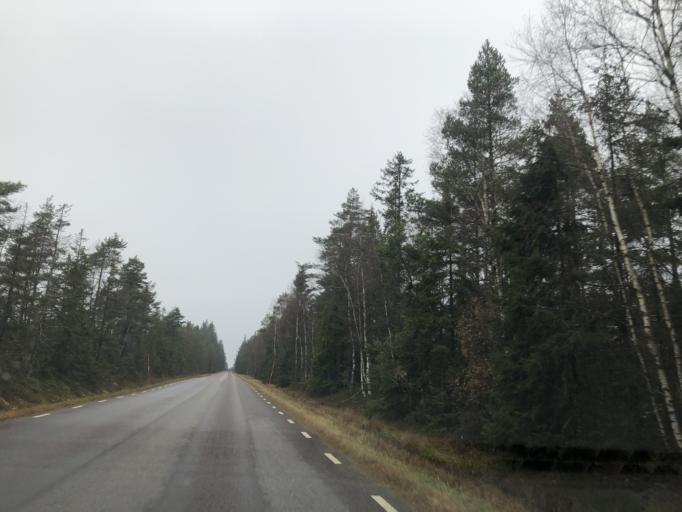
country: SE
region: Vaestra Goetaland
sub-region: Ulricehamns Kommun
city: Ulricehamn
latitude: 57.7561
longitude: 13.5054
